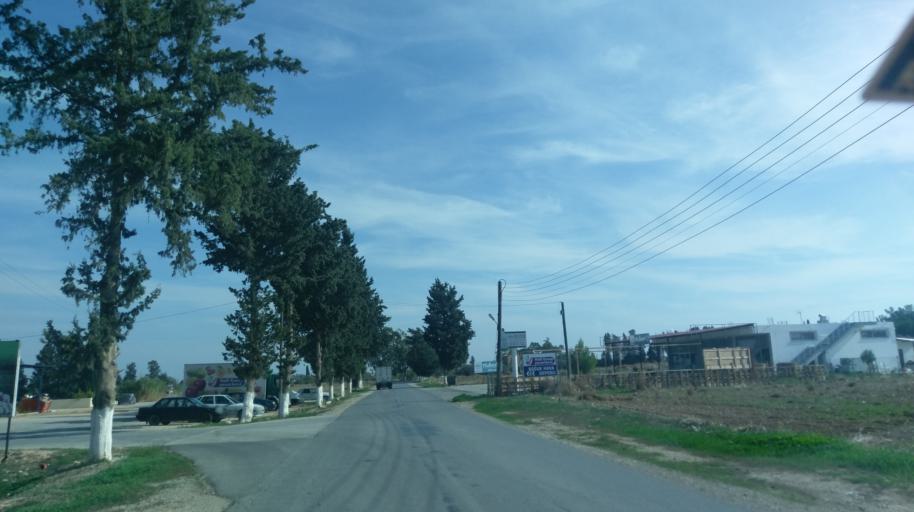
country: CY
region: Larnaka
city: Pergamos
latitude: 35.1067
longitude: 33.7066
